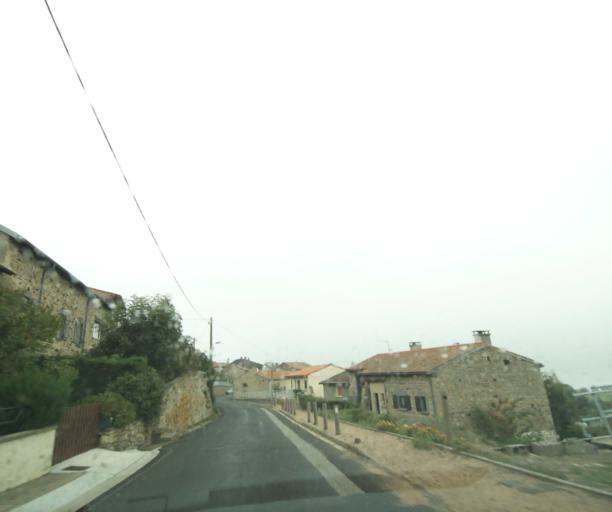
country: FR
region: Auvergne
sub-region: Departement du Puy-de-Dome
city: Ceyrat
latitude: 45.7237
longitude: 3.0458
